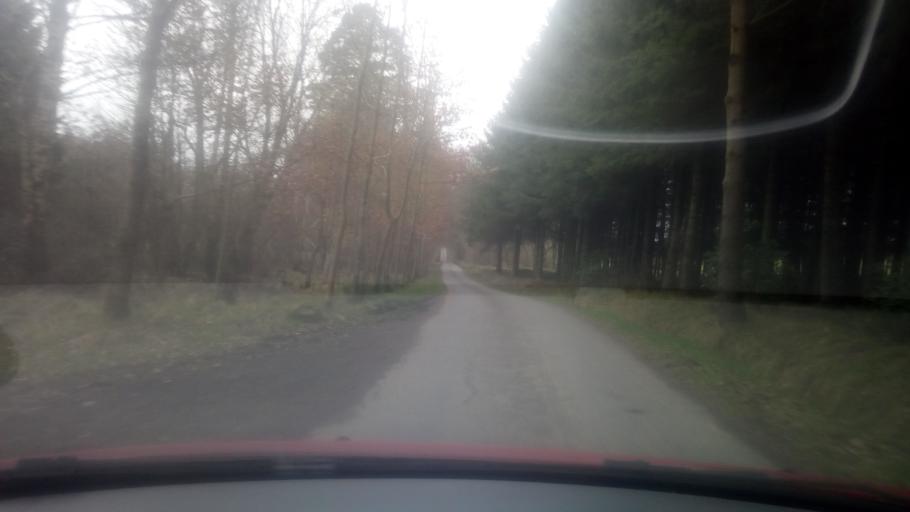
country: GB
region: Scotland
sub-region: The Scottish Borders
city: Jedburgh
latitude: 55.4346
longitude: -2.6401
